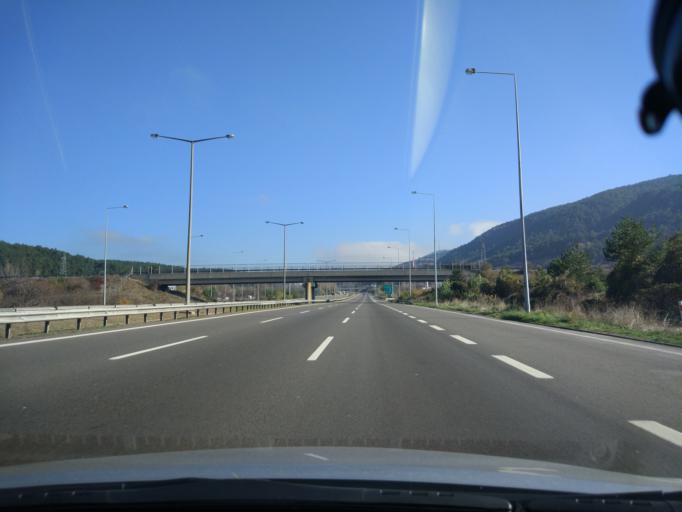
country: TR
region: Bolu
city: Yenicaga
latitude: 40.7427
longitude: 31.8557
